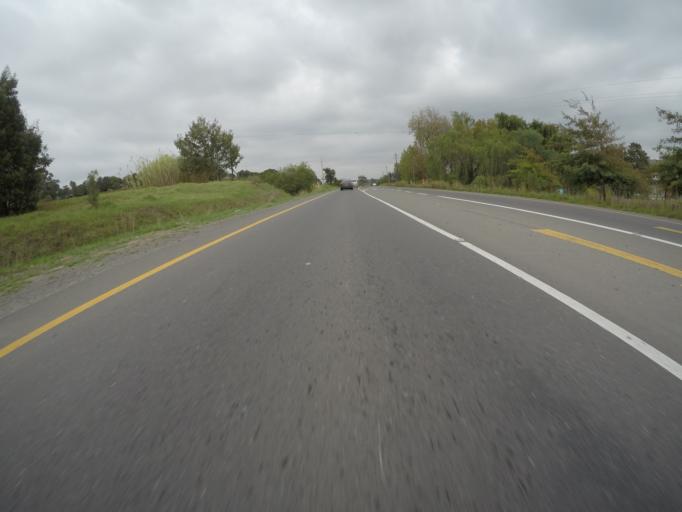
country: ZA
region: Western Cape
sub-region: City of Cape Town
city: Kraaifontein
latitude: -33.8392
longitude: 18.6048
